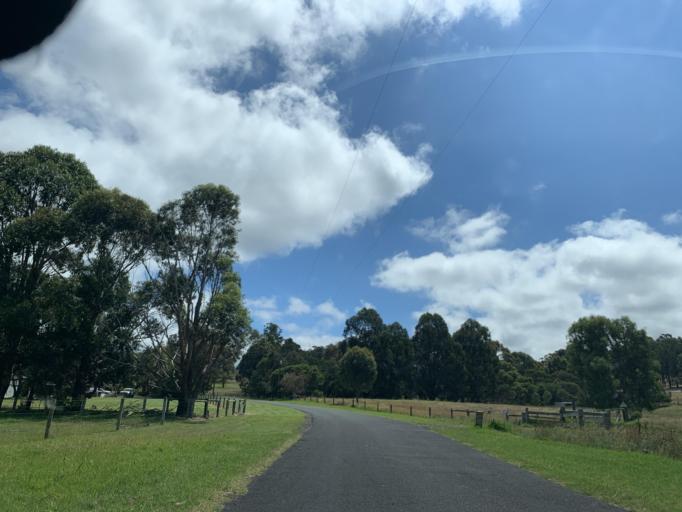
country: AU
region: Victoria
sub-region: Wellington
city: Heyfield
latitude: -38.0275
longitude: 146.6327
